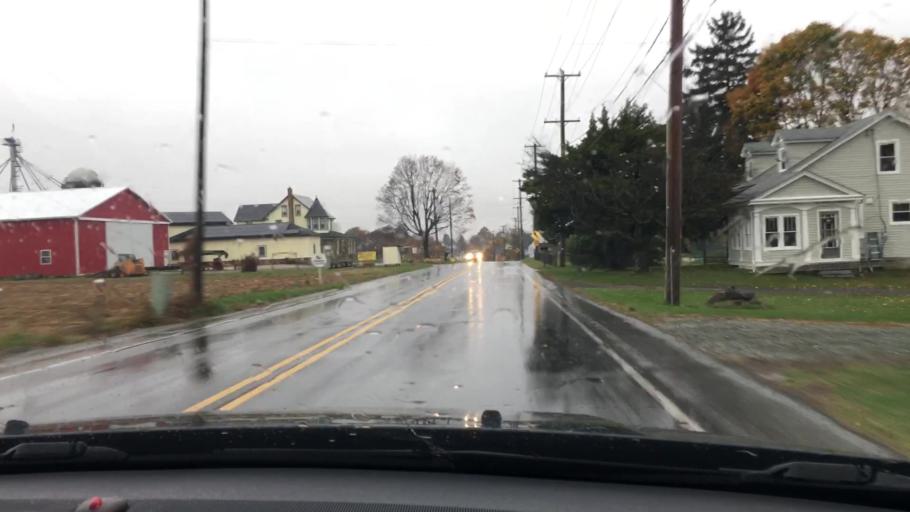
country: US
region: Pennsylvania
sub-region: York County
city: Susquehanna Trails
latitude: 39.8166
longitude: -76.3845
